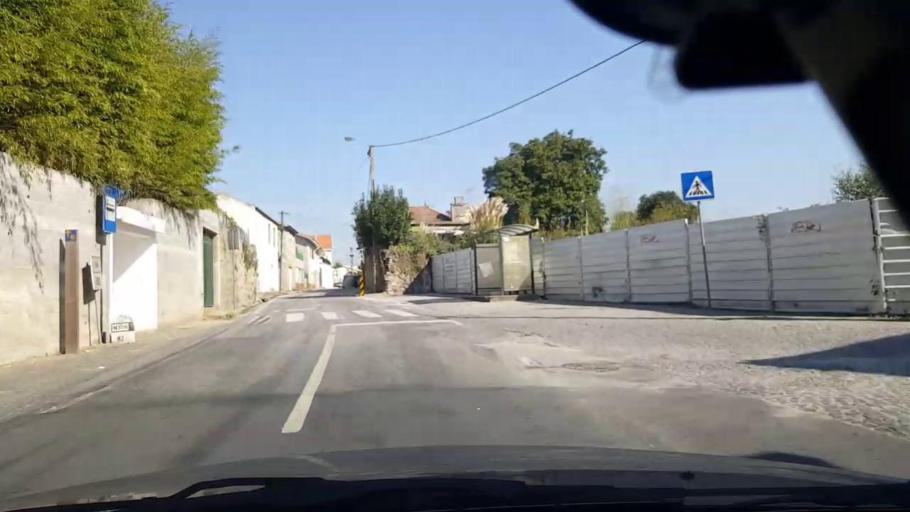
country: PT
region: Porto
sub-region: Maia
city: Gemunde
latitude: 41.3041
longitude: -8.6787
